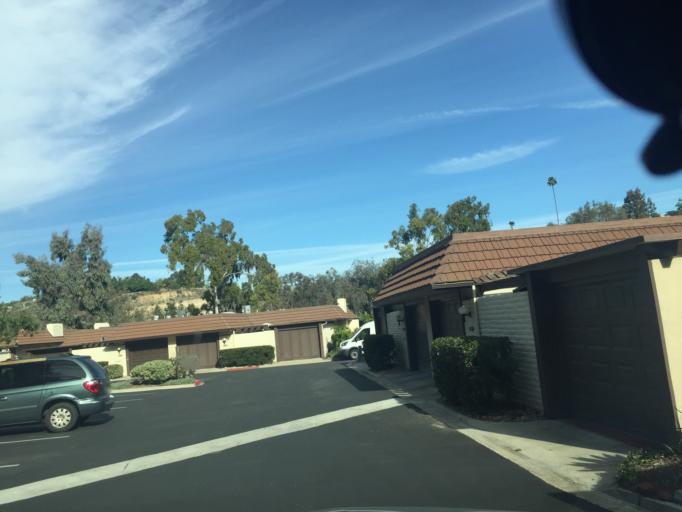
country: US
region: California
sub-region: San Diego County
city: Lemon Grove
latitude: 32.7671
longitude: -117.0854
